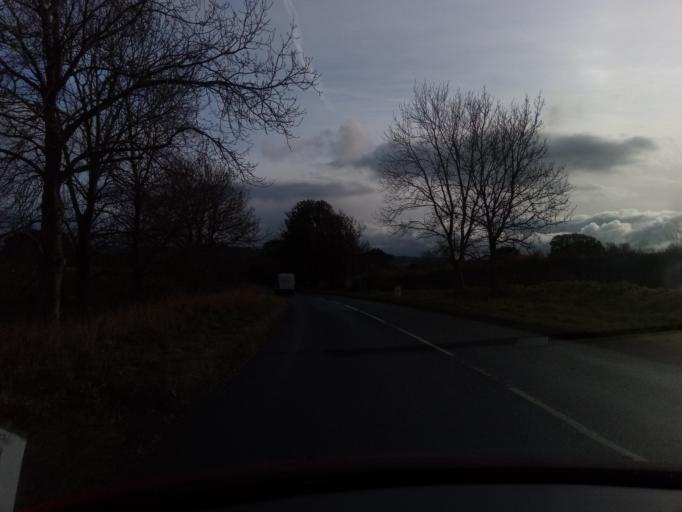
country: GB
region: England
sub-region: Northumberland
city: Wall
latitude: 55.0438
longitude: -2.1505
